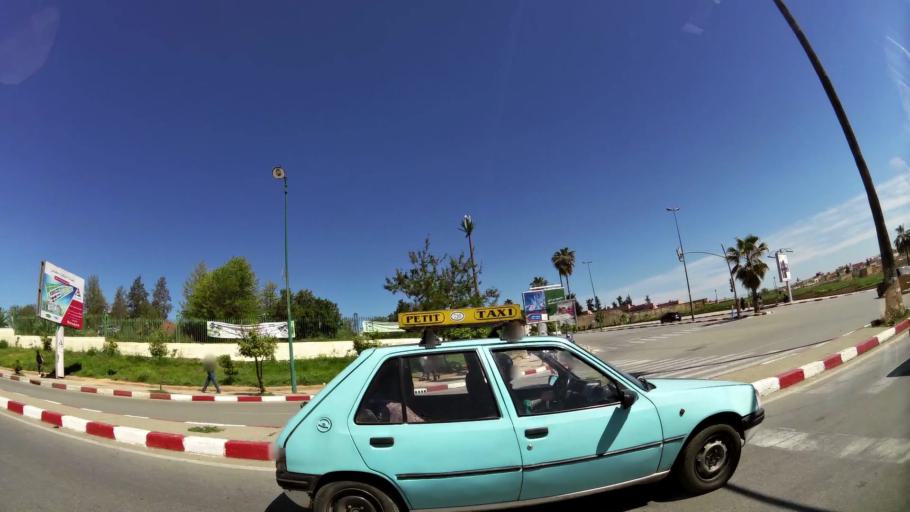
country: MA
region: Meknes-Tafilalet
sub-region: Meknes
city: Meknes
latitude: 33.8835
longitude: -5.5708
